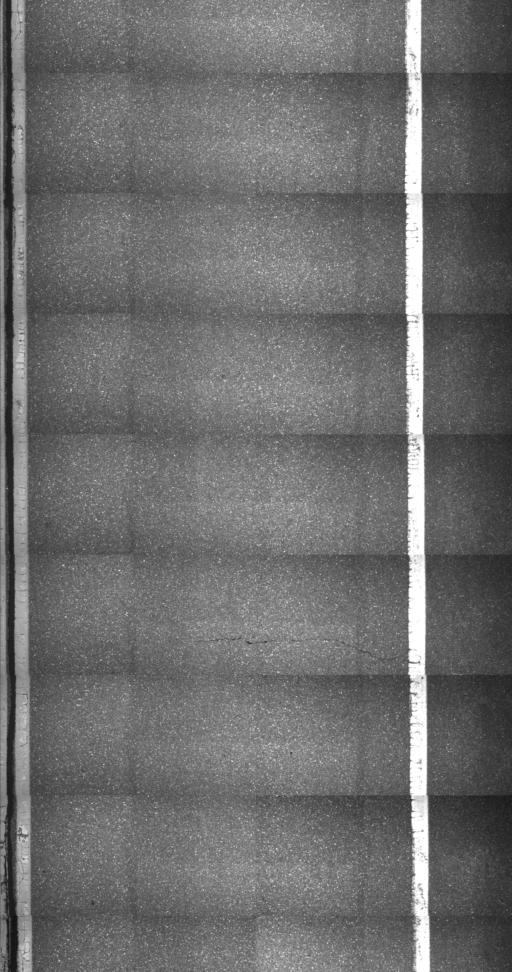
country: US
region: Vermont
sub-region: Orleans County
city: Newport
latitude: 45.0009
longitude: -72.4121
